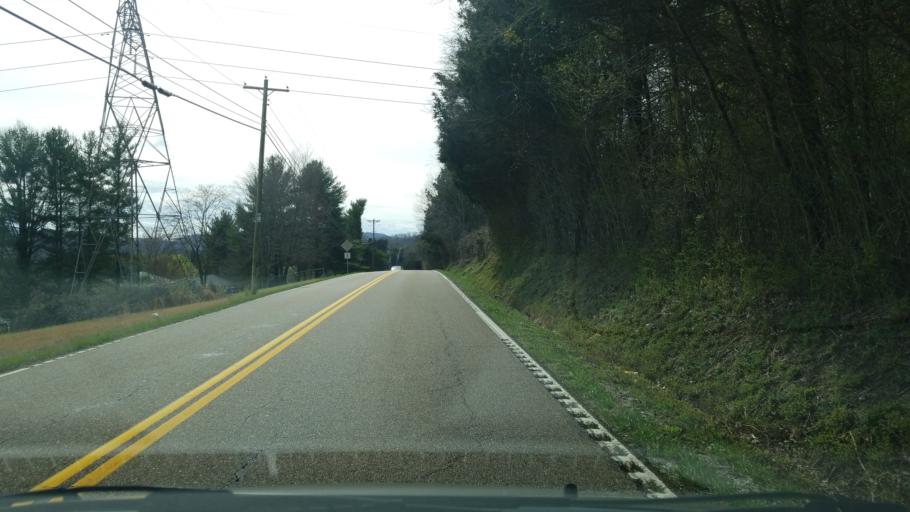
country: US
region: Tennessee
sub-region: Hamilton County
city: Collegedale
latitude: 35.1140
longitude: -85.0668
